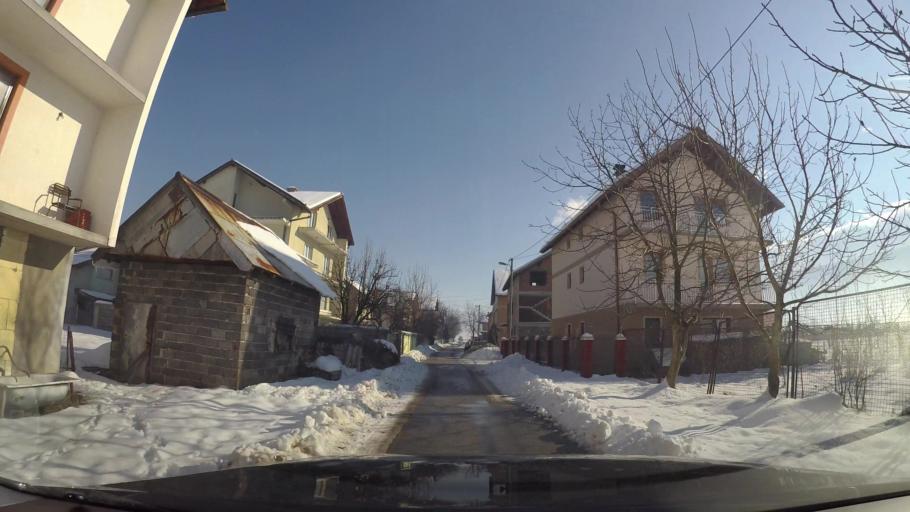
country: BA
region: Federation of Bosnia and Herzegovina
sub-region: Kanton Sarajevo
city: Sarajevo
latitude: 43.8073
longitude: 18.3151
